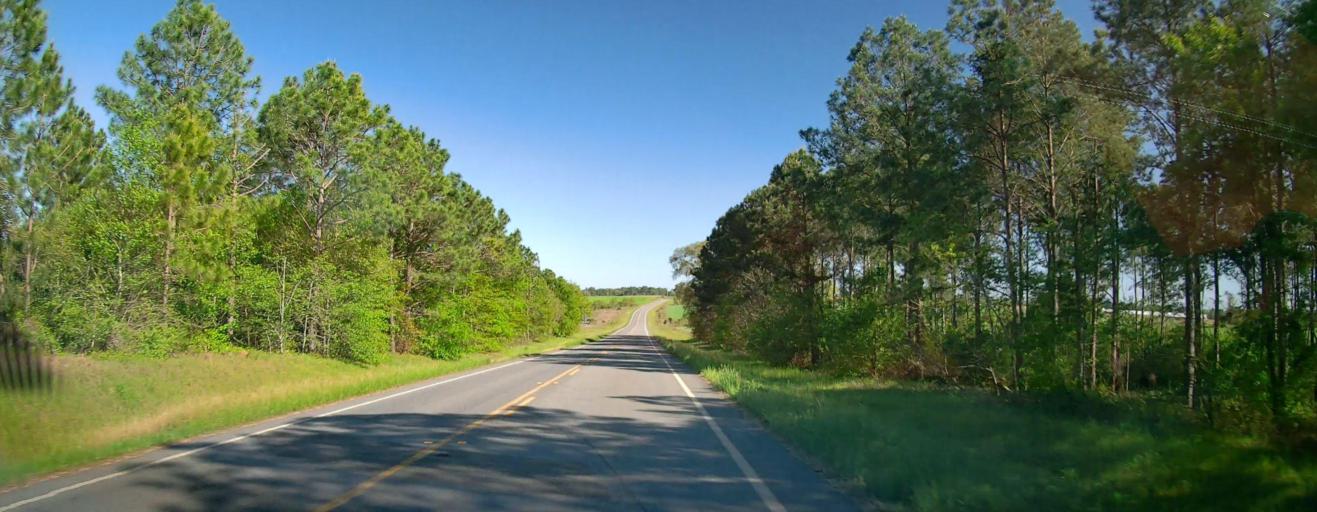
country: US
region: Georgia
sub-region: Wilcox County
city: Rochelle
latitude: 31.9887
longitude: -83.4650
